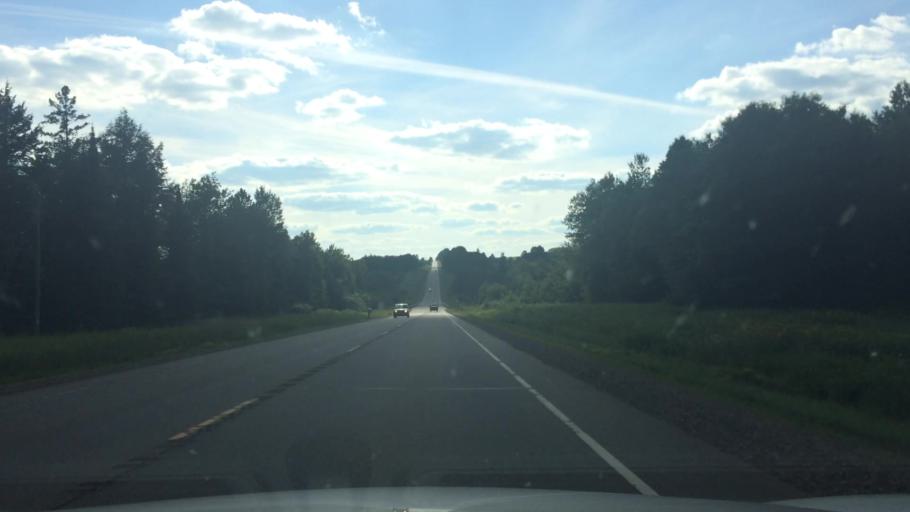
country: US
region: Wisconsin
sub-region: Lincoln County
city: Merrill
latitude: 45.1780
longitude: -89.5897
